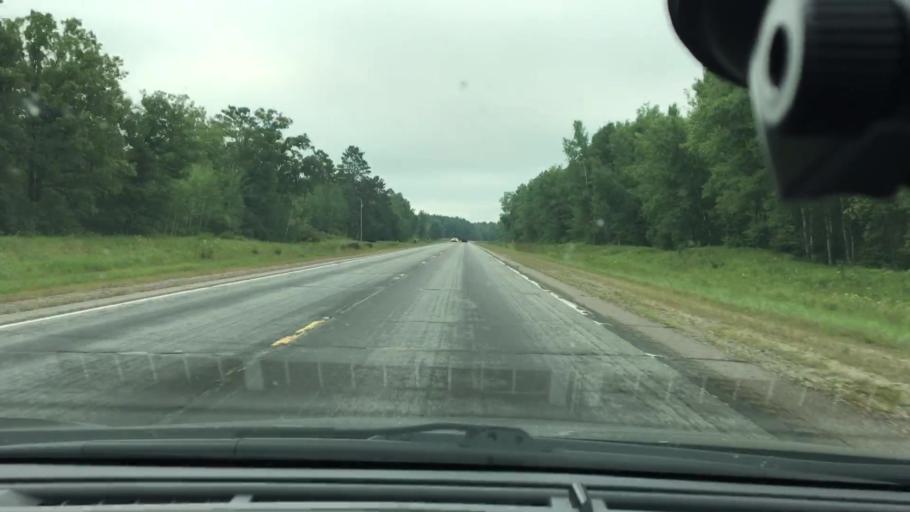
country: US
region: Minnesota
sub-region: Crow Wing County
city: Cross Lake
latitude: 46.6764
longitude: -93.9525
